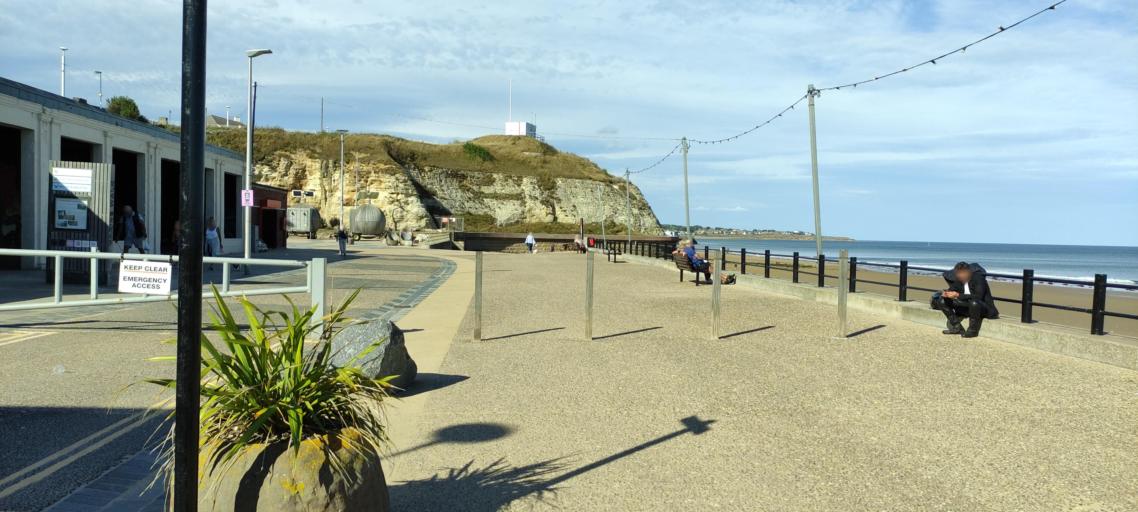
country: GB
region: England
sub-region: Sunderland
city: Sunderland
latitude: 54.9252
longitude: -1.3658
